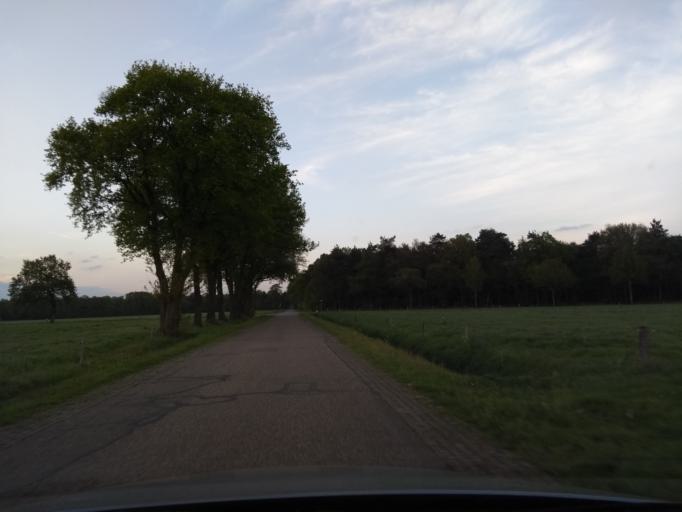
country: NL
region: Overijssel
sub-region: Gemeente Hof van Twente
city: Hengevelde
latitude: 52.2096
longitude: 6.6892
